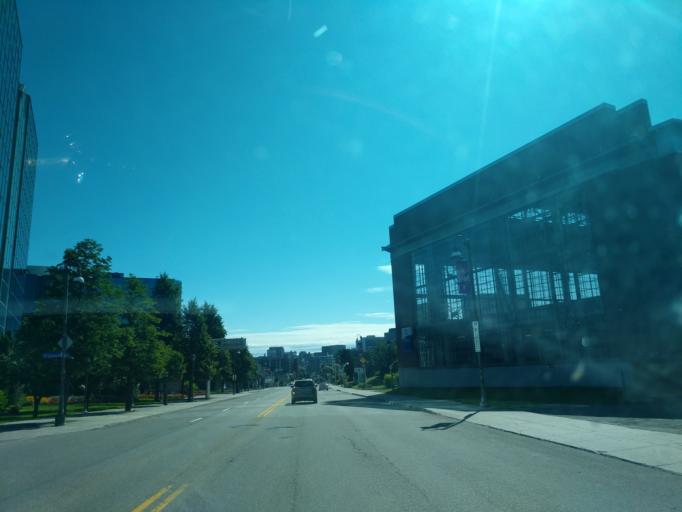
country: CA
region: Ontario
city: Ottawa
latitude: 45.4310
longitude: -75.7316
